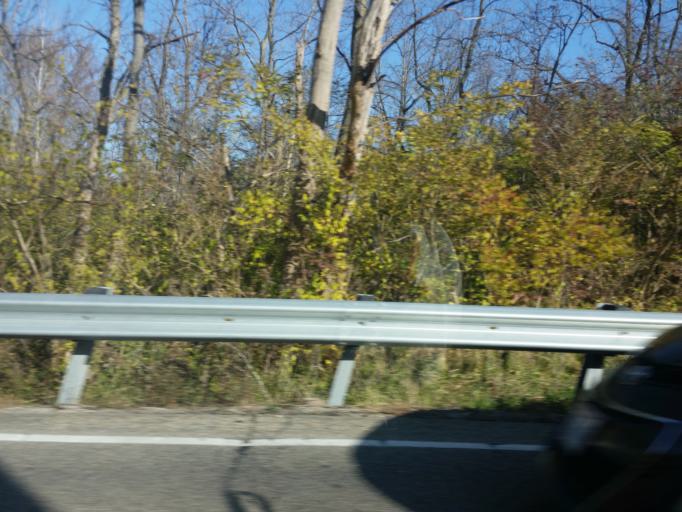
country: US
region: Ohio
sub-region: Butler County
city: Oxford
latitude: 39.4710
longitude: -84.7042
